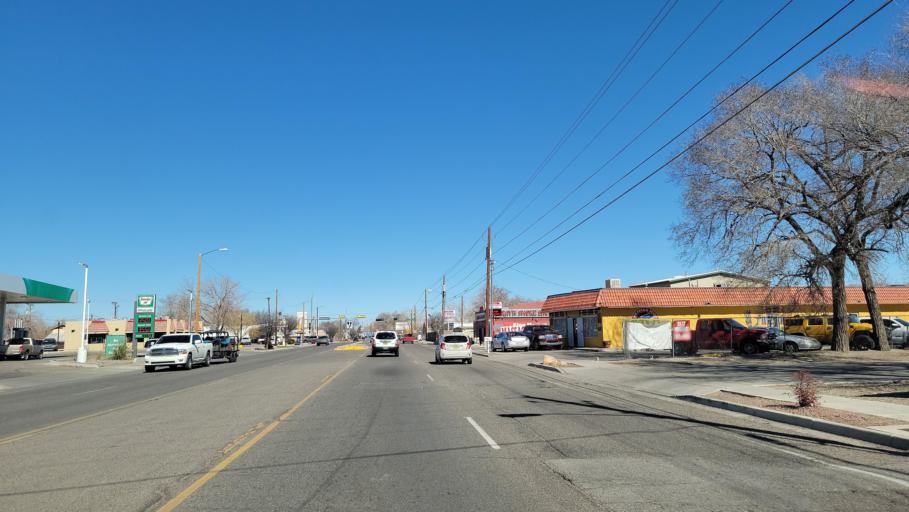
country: US
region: New Mexico
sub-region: Bernalillo County
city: South Valley
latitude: 35.0293
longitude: -106.6799
